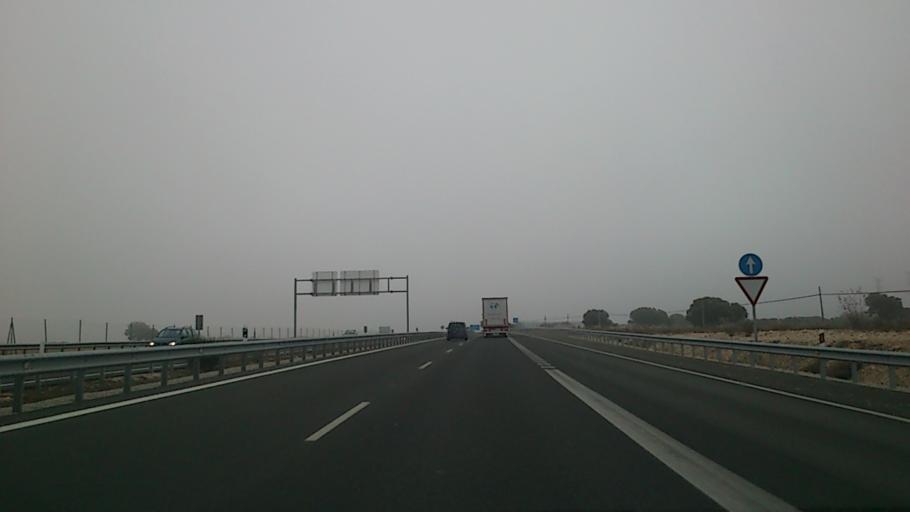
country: ES
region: Castille-La Mancha
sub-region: Provincia de Guadalajara
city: Ledanca
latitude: 40.8644
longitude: -2.8276
